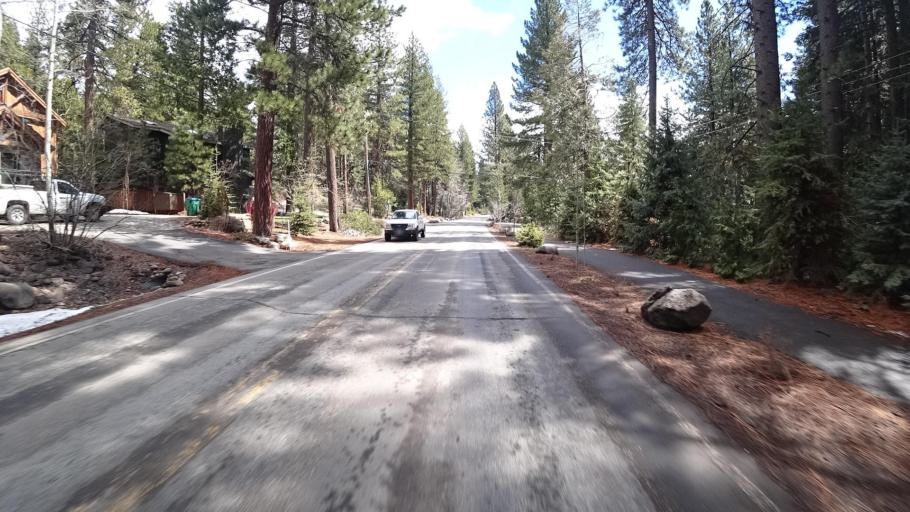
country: US
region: Nevada
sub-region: Washoe County
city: Incline Village
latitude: 39.2498
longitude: -119.9786
